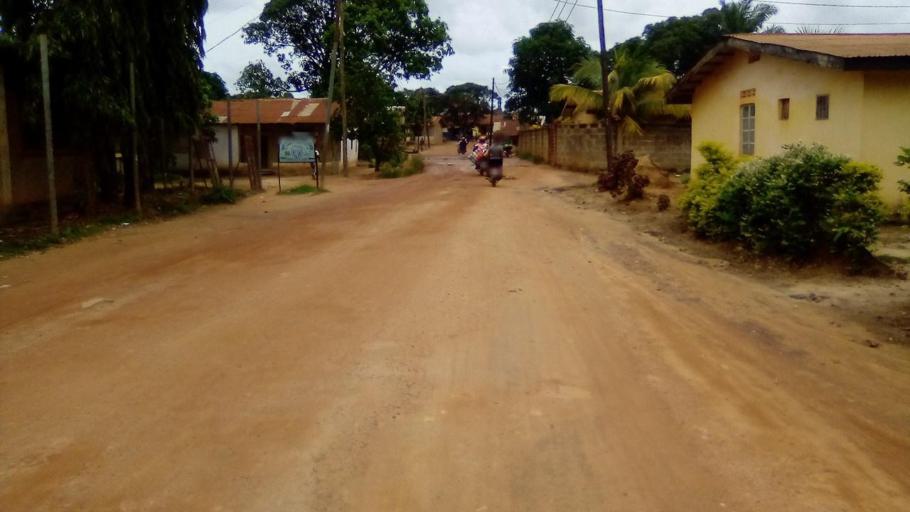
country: SL
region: Southern Province
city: Bo
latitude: 7.9457
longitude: -11.7391
